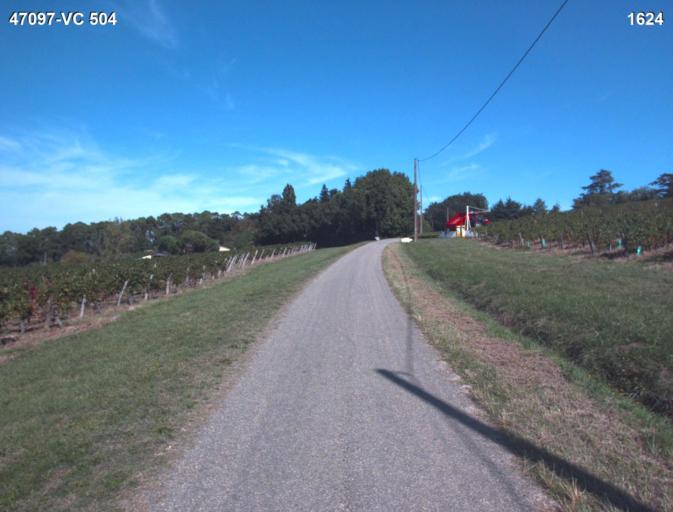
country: FR
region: Aquitaine
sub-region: Departement du Lot-et-Garonne
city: Vianne
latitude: 44.1820
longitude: 0.3426
